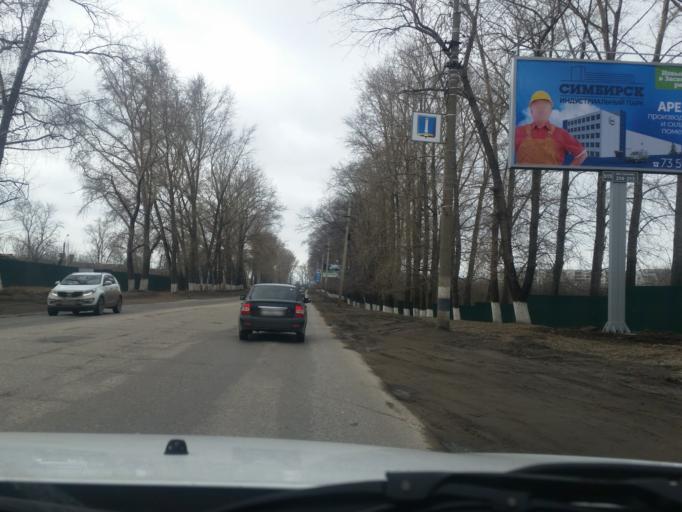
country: RU
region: Ulyanovsk
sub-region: Ulyanovskiy Rayon
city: Ulyanovsk
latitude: 54.3298
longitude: 48.4948
